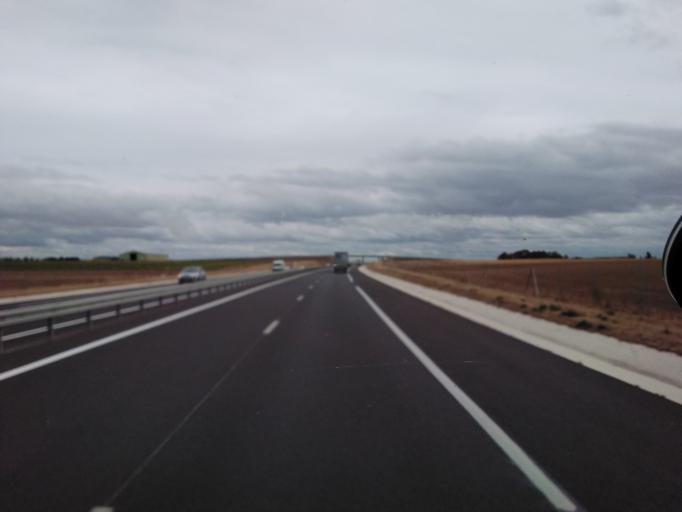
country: FR
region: Champagne-Ardenne
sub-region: Departement de la Marne
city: Sarry
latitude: 48.9057
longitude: 4.4431
